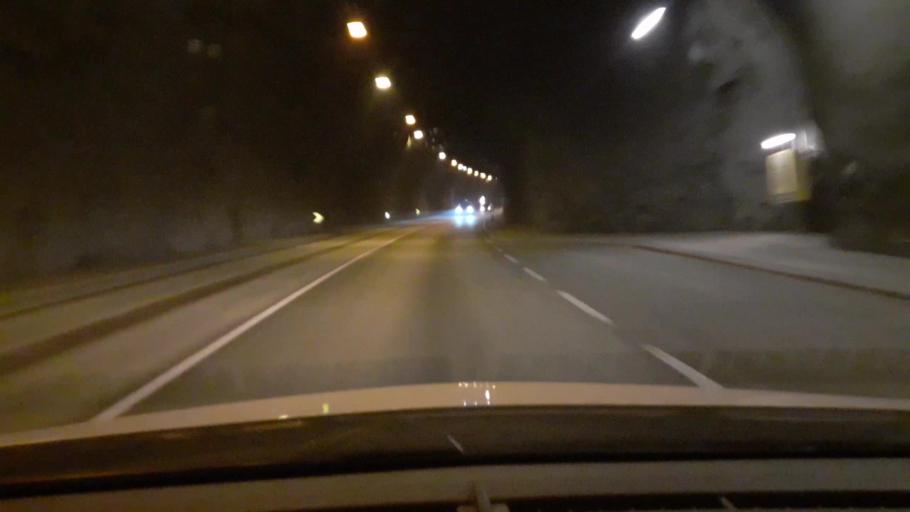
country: IS
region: Capital Region
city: Reykjavik
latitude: 64.2848
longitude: -21.8456
